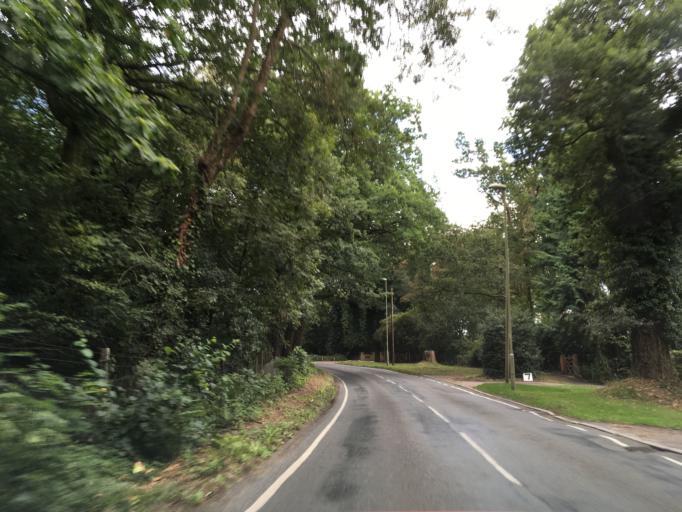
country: GB
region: England
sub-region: Hampshire
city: Chandlers Ford
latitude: 50.9991
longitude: -1.3606
